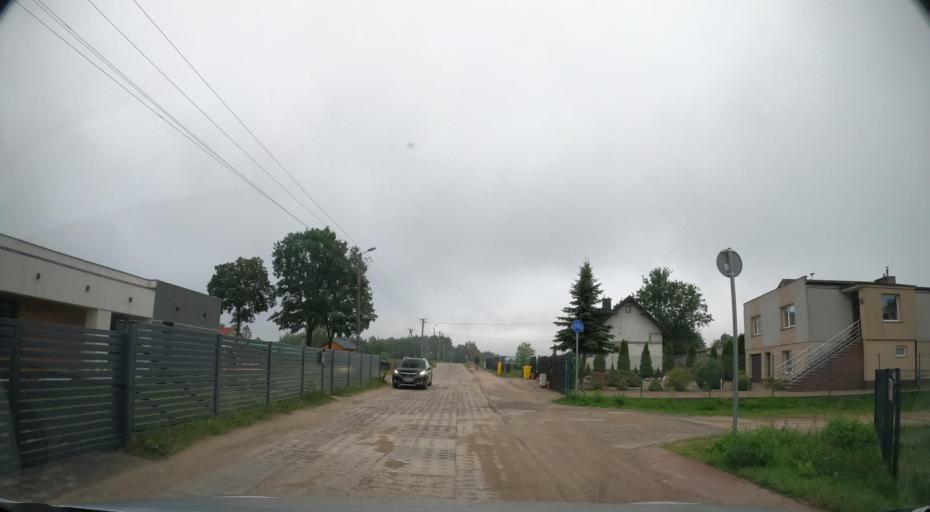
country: PL
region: Pomeranian Voivodeship
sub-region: Powiat kartuski
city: Chwaszczyno
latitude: 54.4283
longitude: 18.4161
